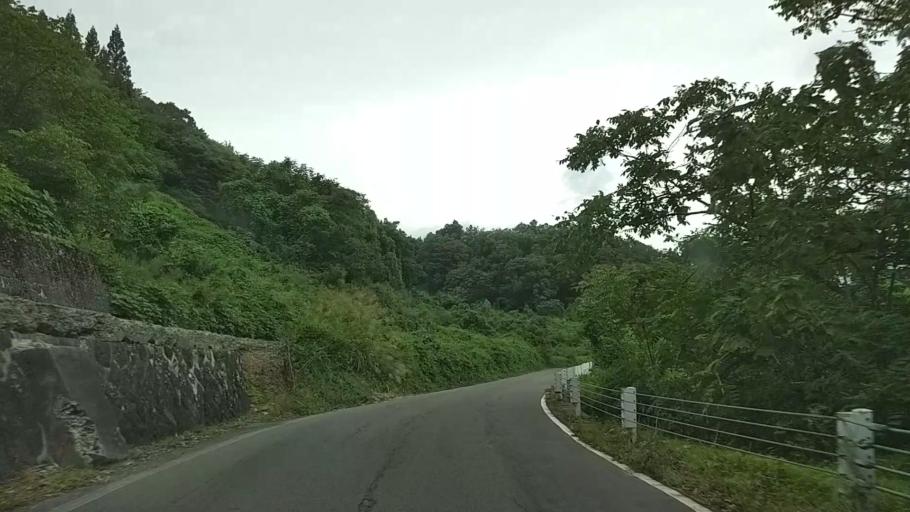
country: JP
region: Nagano
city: Iiyama
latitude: 36.8001
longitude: 138.3436
